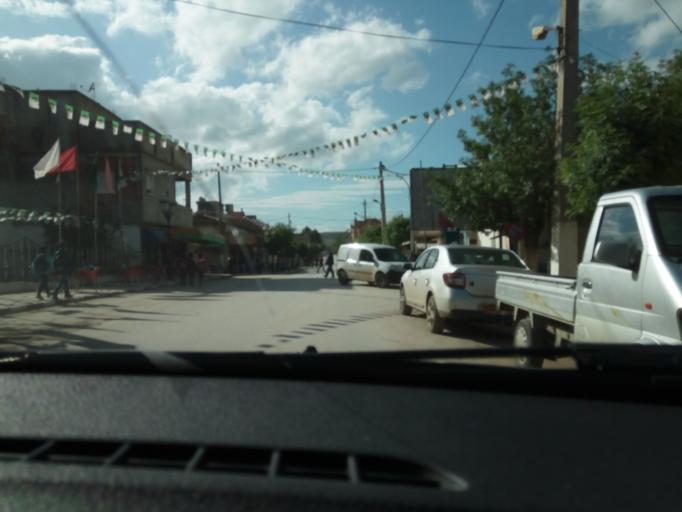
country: DZ
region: Tipaza
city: Hadjout
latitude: 36.3702
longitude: 2.4767
